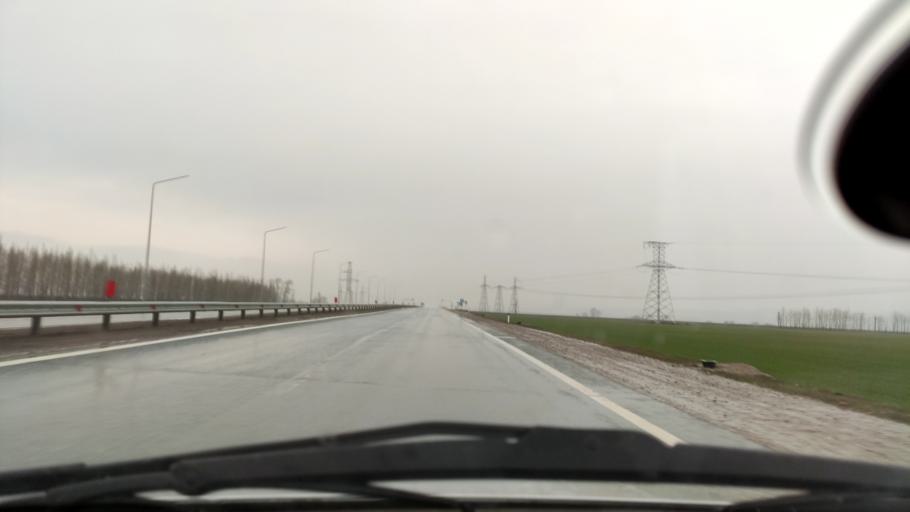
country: RU
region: Bashkortostan
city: Tolbazy
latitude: 54.2440
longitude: 55.8826
